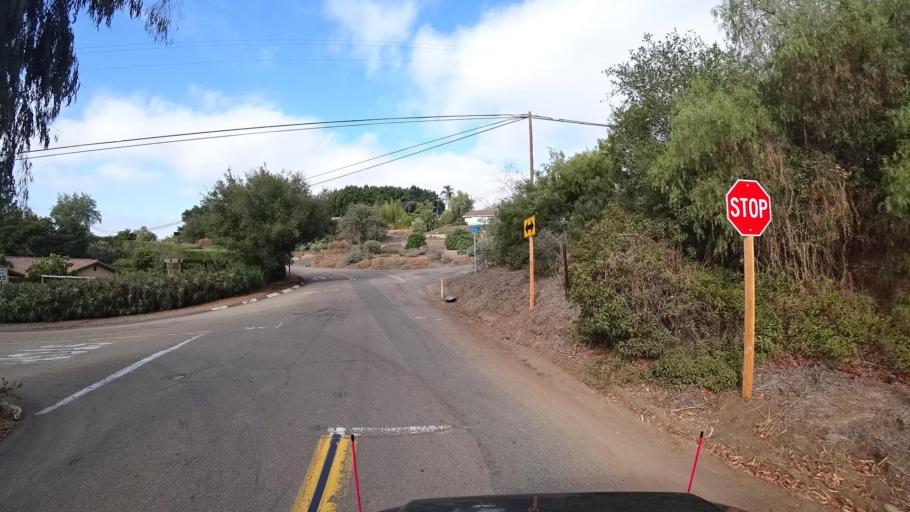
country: US
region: California
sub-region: San Diego County
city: Vista
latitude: 33.2010
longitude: -117.2116
